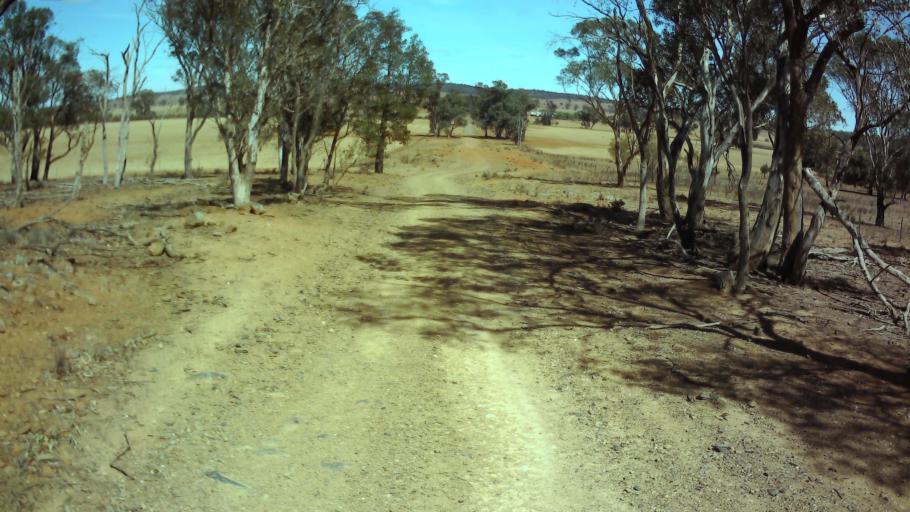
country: AU
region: New South Wales
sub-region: Forbes
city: Forbes
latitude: -33.7166
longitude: 147.8099
